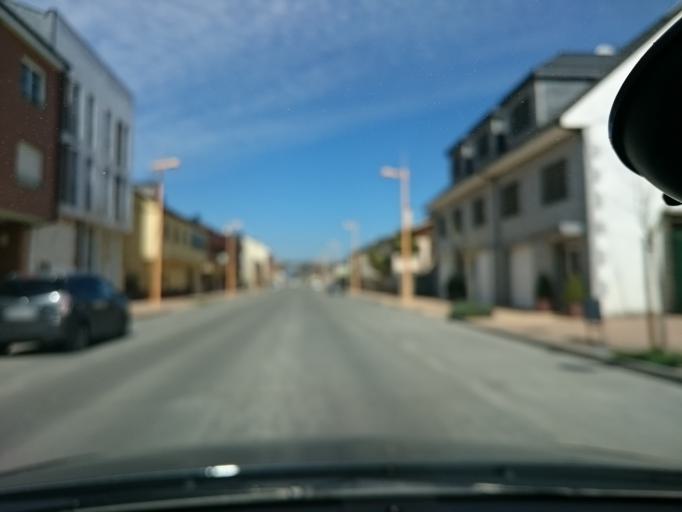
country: ES
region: Castille and Leon
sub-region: Provincia de Leon
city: Camponaraya
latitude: 42.5720
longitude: -6.6397
